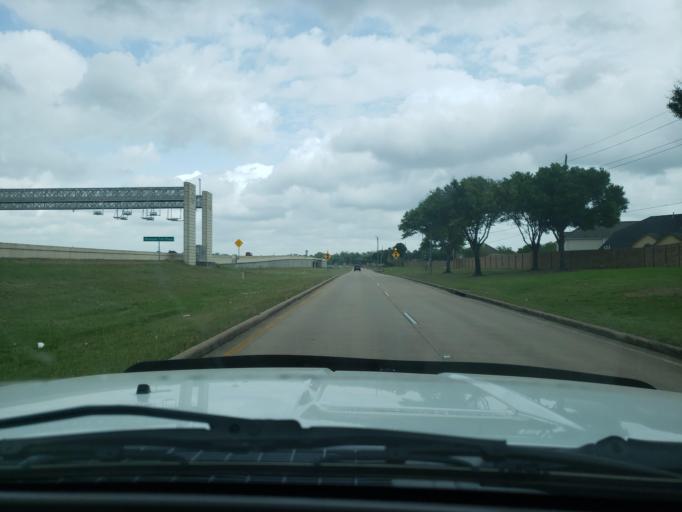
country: US
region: Texas
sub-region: Fort Bend County
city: Greatwood
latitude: 29.5715
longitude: -95.6828
